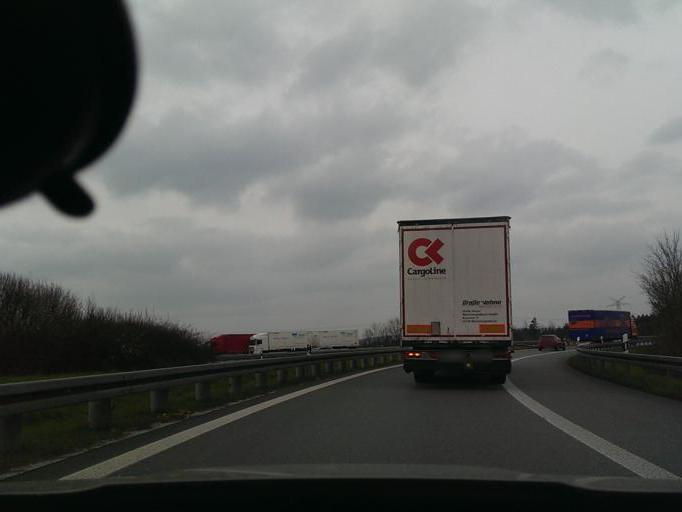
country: DE
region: North Rhine-Westphalia
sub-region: Regierungsbezirk Detmold
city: Verl
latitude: 51.9442
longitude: 8.5472
